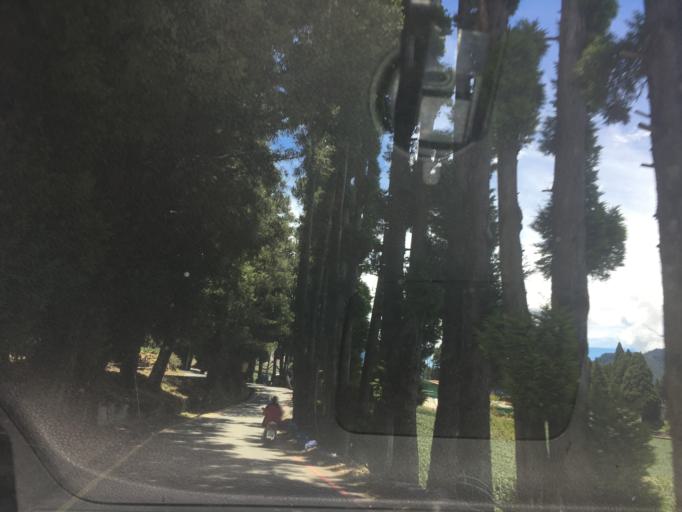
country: TW
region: Taiwan
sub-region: Nantou
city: Puli
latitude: 24.2444
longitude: 121.2433
